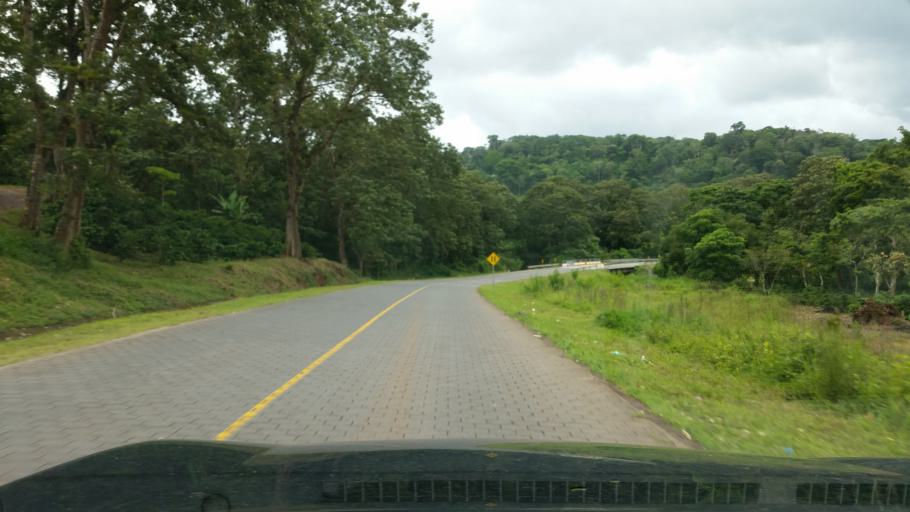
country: NI
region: Jinotega
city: Jinotega
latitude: 13.1960
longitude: -85.7339
